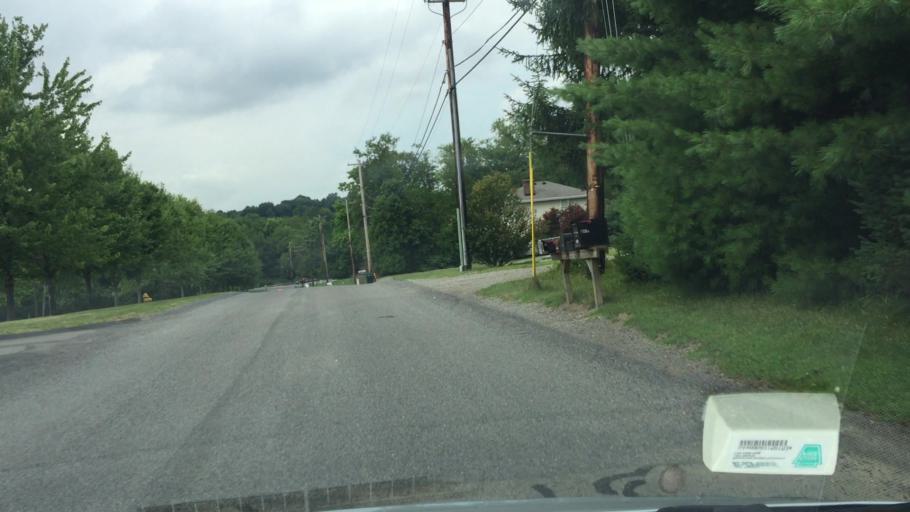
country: US
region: Pennsylvania
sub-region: Allegheny County
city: Allison Park
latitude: 40.5910
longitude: -79.9654
